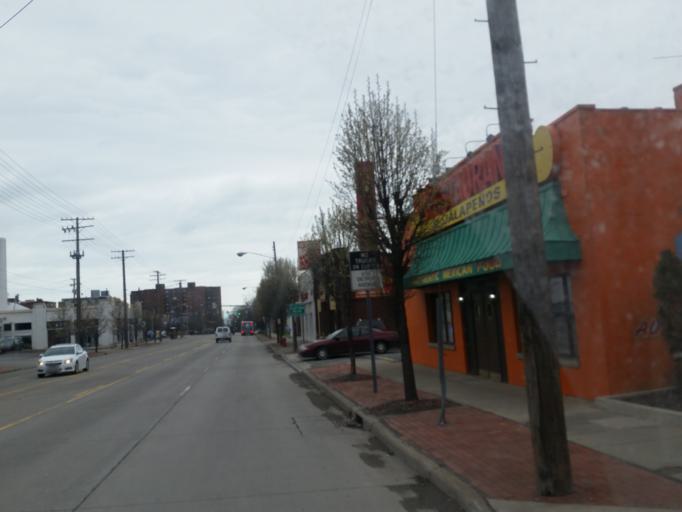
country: US
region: Ohio
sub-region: Cuyahoga County
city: Lakewood
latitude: 41.4857
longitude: -81.7686
